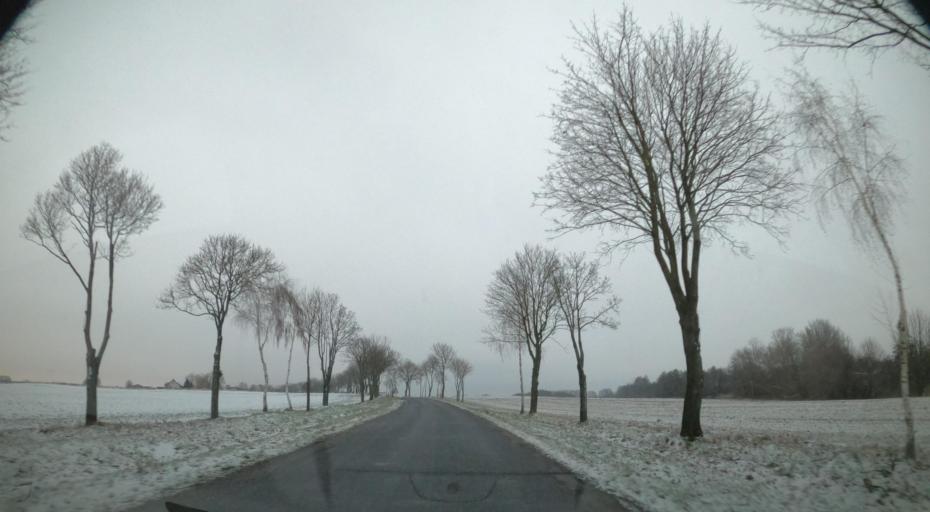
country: PL
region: Kujawsko-Pomorskie
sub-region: Powiat lipnowski
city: Wielgie
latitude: 52.7031
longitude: 19.2881
